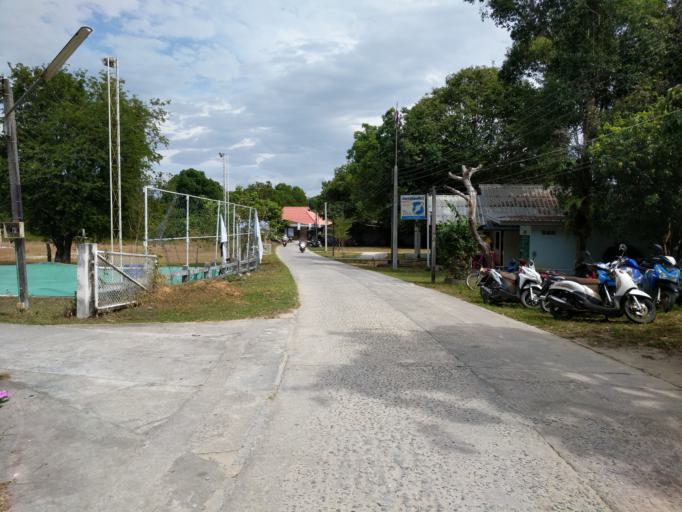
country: TH
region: Ranong
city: Kapoe
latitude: 9.7399
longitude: 98.4196
